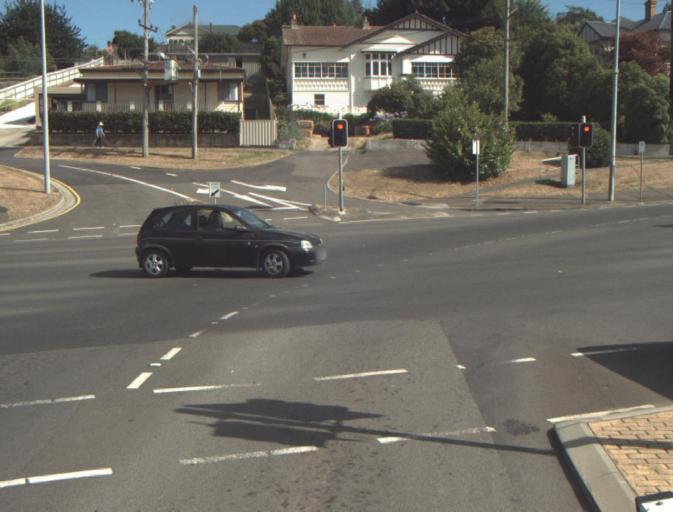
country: AU
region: Tasmania
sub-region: Launceston
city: Newnham
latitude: -41.4096
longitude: 147.1320
